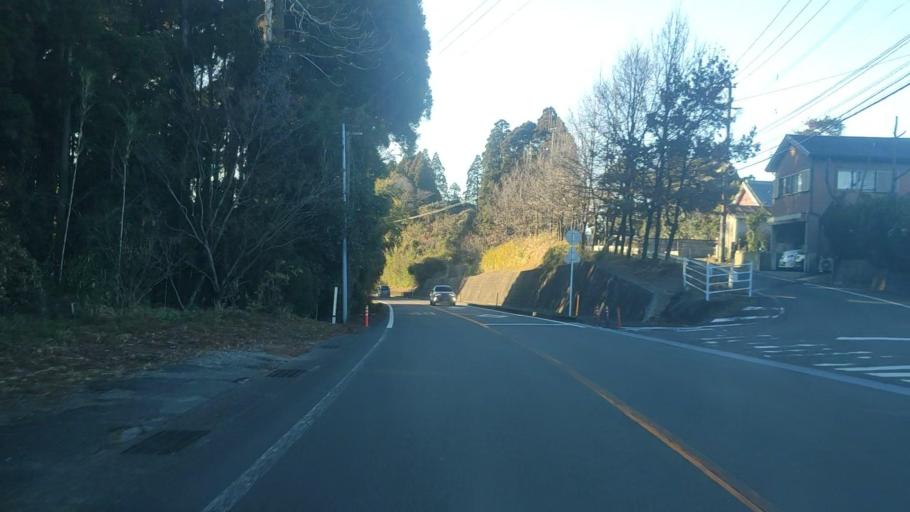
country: JP
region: Miyazaki
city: Miyazaki-shi
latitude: 31.8591
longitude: 131.3745
